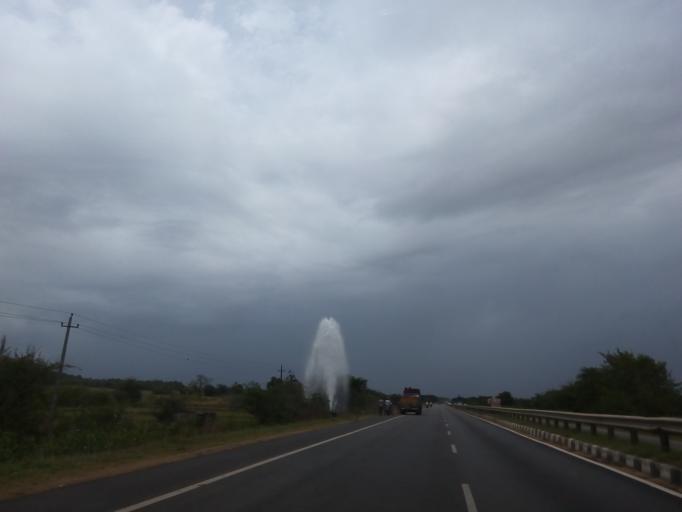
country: IN
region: Karnataka
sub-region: Davanagere
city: Harihar
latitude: 14.4755
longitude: 75.8225
